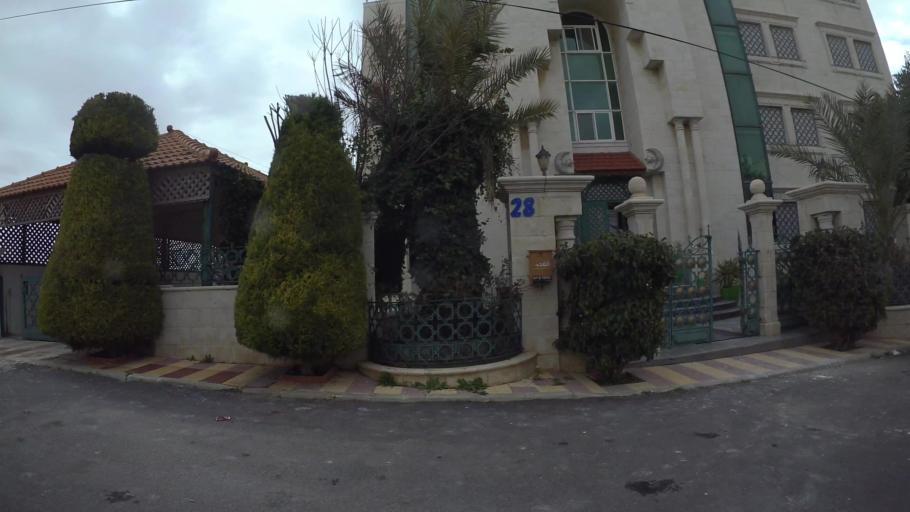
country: JO
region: Amman
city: Umm as Summaq
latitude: 31.9115
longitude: 35.8455
